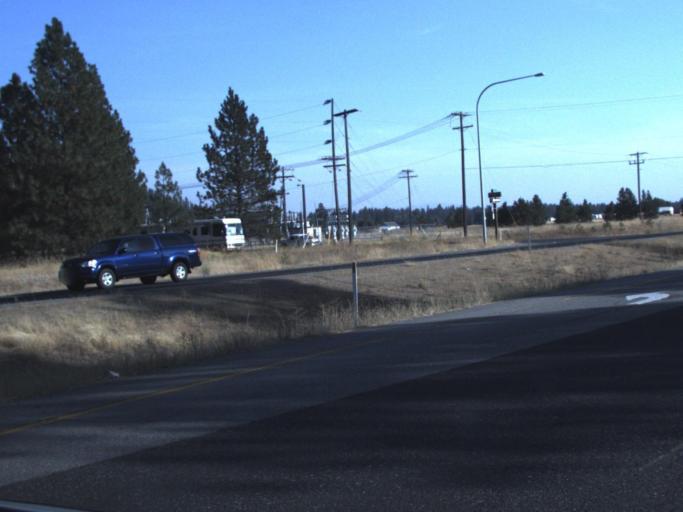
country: US
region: Washington
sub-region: Spokane County
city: Mead
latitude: 47.8386
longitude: -117.3542
